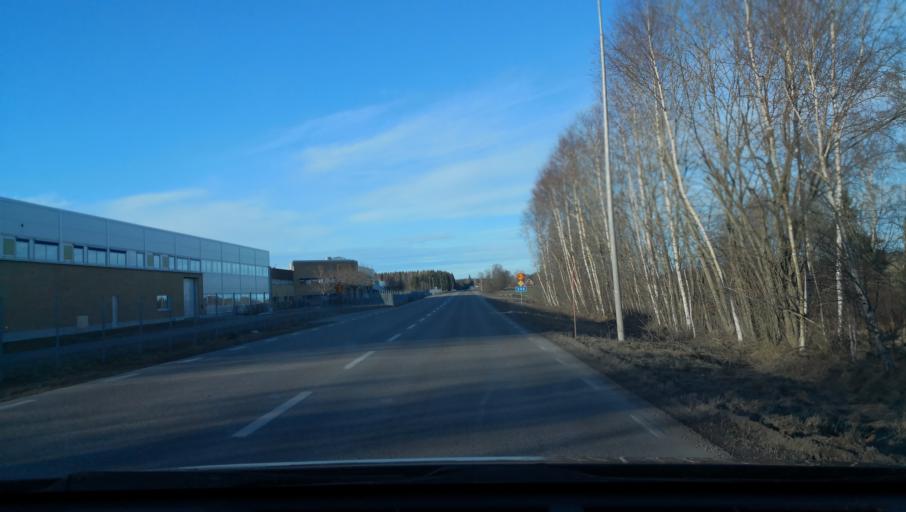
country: SE
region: Uppsala
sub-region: Osthammars Kommun
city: Gimo
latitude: 60.1791
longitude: 18.1905
